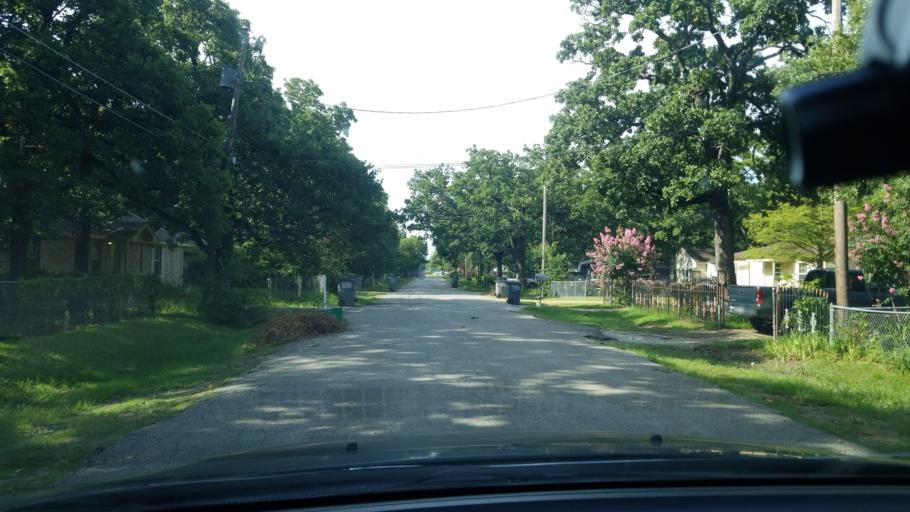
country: US
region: Texas
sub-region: Dallas County
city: Balch Springs
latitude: 32.7217
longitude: -96.6365
